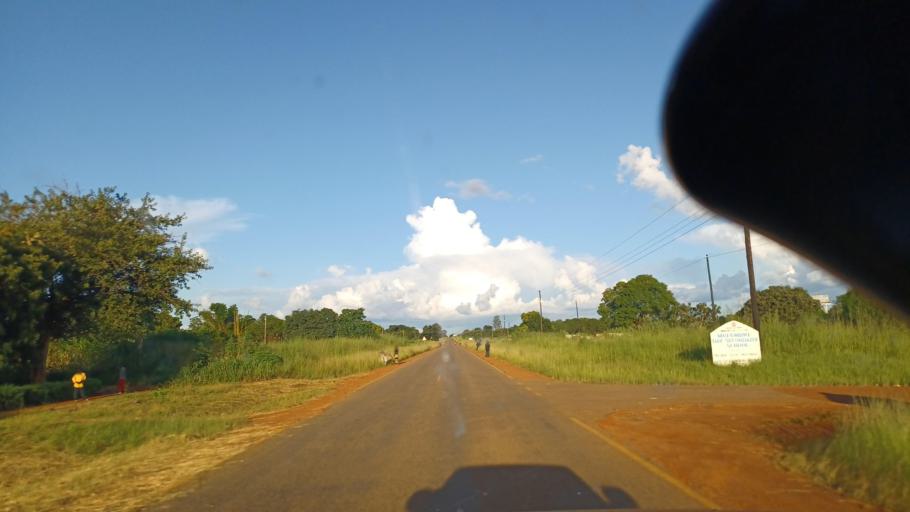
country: ZM
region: North-Western
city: Kalengwa
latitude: -13.1427
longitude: 25.0308
